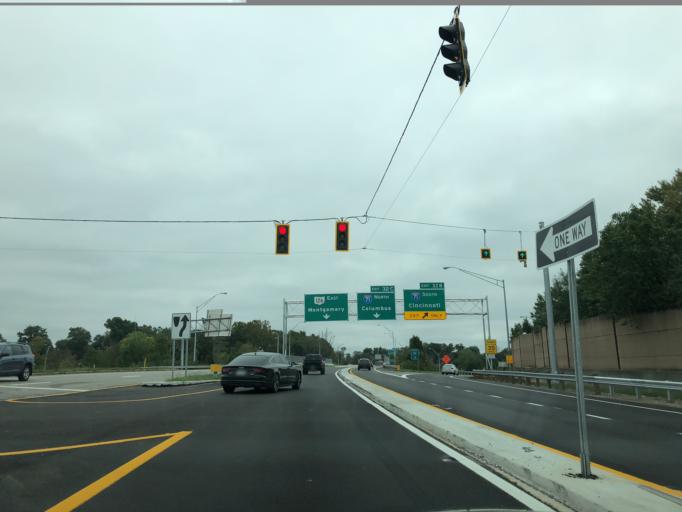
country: US
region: Ohio
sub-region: Hamilton County
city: Blue Ash
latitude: 39.2260
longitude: -84.3690
